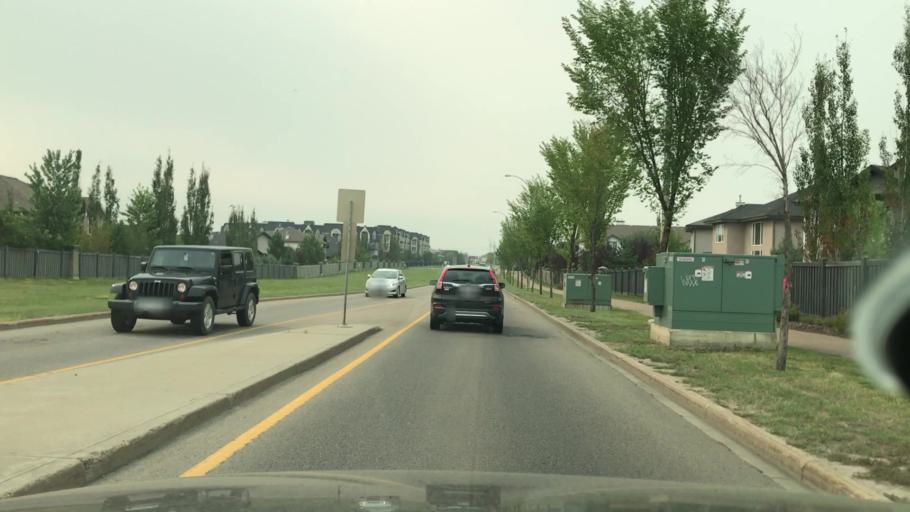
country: CA
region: Alberta
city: Edmonton
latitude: 53.4442
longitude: -113.5657
